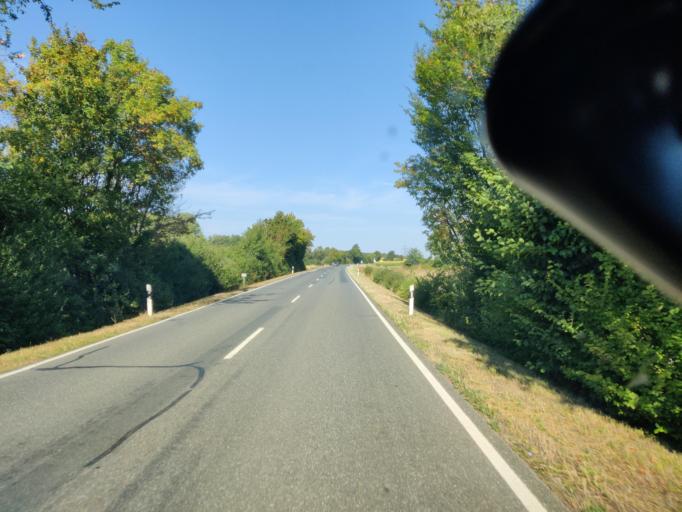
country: DE
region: Bavaria
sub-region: Regierungsbezirk Mittelfranken
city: Hilpoltstein
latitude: 49.1681
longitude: 11.2378
